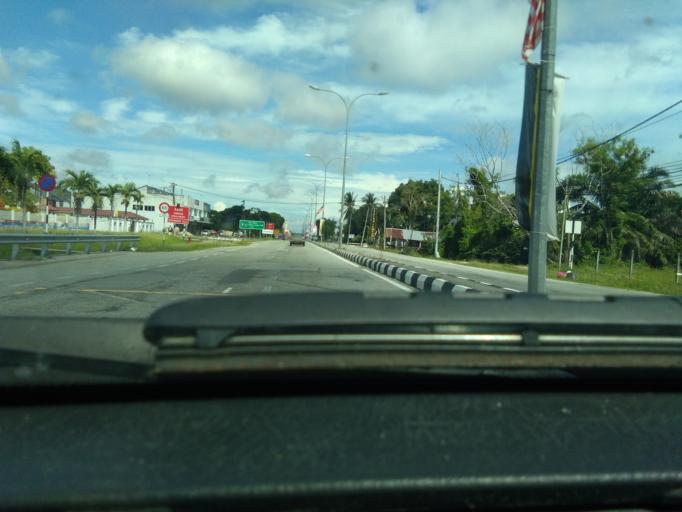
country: MY
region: Perak
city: Bagan Serai
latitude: 5.0062
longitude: 100.5432
